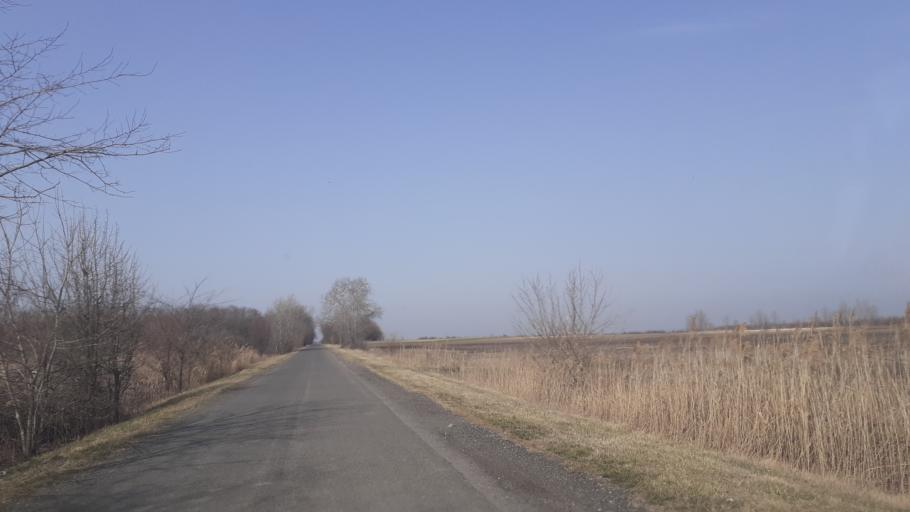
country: HU
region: Pest
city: Dabas
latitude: 47.1193
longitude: 19.2146
